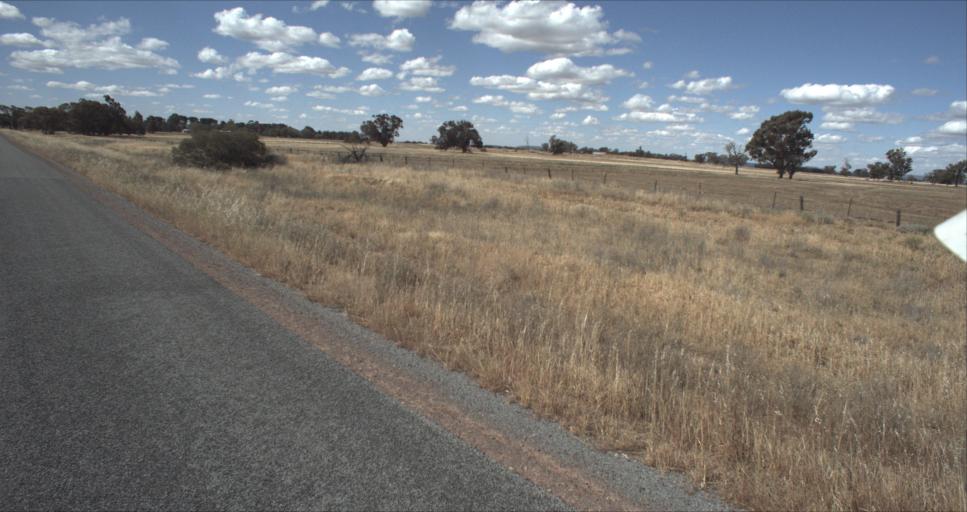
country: AU
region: New South Wales
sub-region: Leeton
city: Leeton
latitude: -34.4905
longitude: 146.2474
